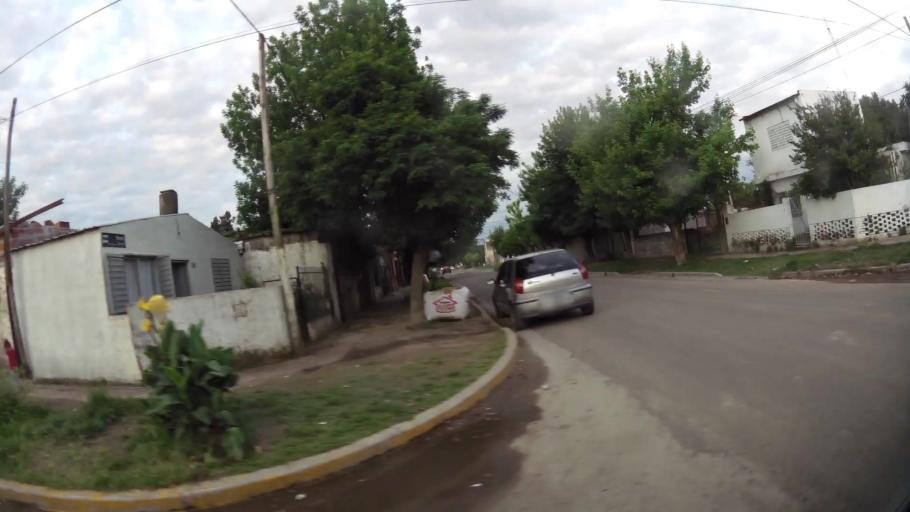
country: AR
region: Buenos Aires
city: San Nicolas de los Arroyos
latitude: -33.3153
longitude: -60.2419
